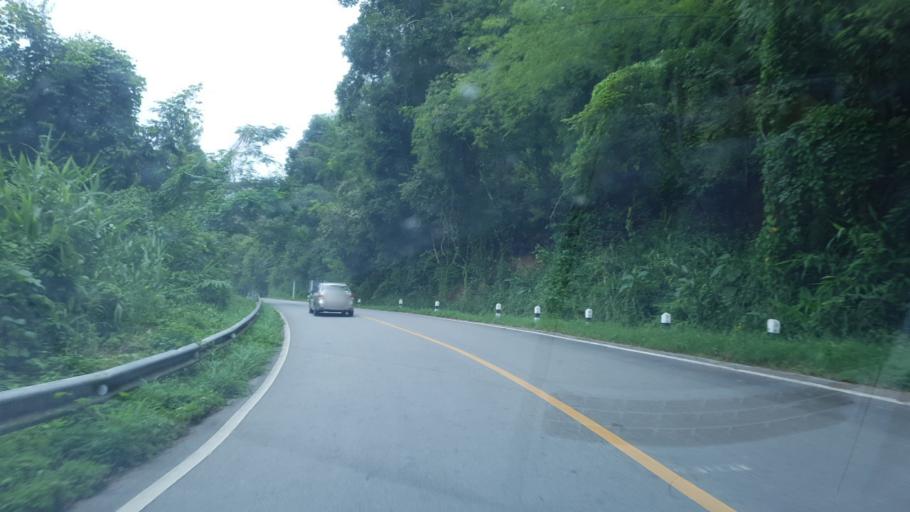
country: TH
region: Mae Hong Son
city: Khun Yuam
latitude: 18.7226
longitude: 97.9078
